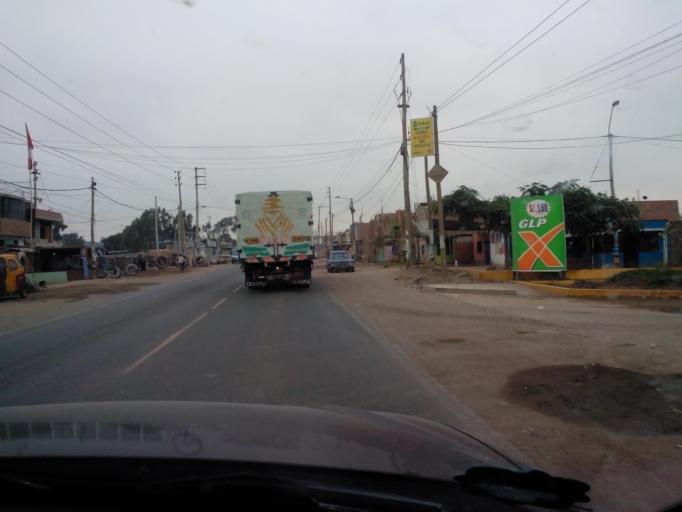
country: PE
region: Ica
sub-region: Provincia de Chincha
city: Chincha Baja
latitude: -13.4463
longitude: -76.1357
